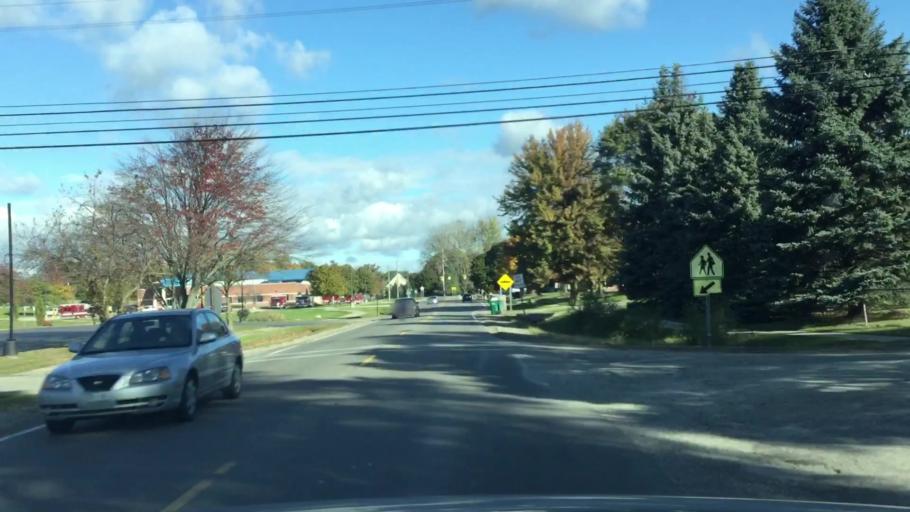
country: US
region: Michigan
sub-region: Oakland County
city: Waterford
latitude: 42.6721
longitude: -83.3867
